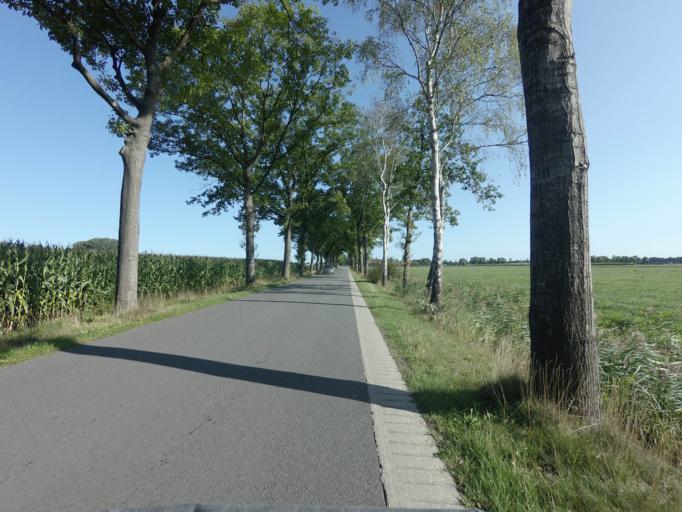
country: NL
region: Overijssel
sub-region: Gemeente Raalte
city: Raalte
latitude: 52.4064
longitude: 6.2845
